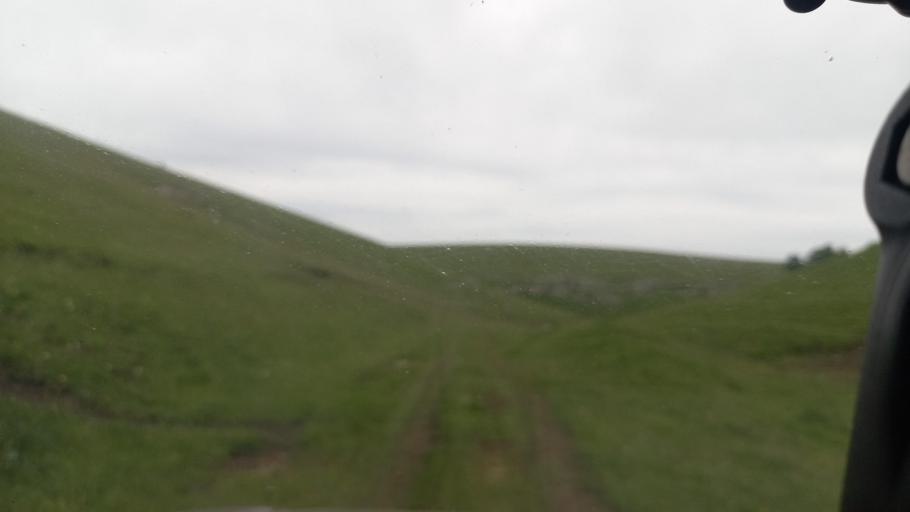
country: RU
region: Karachayevo-Cherkesiya
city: Pregradnaya
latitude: 43.9832
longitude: 41.2979
